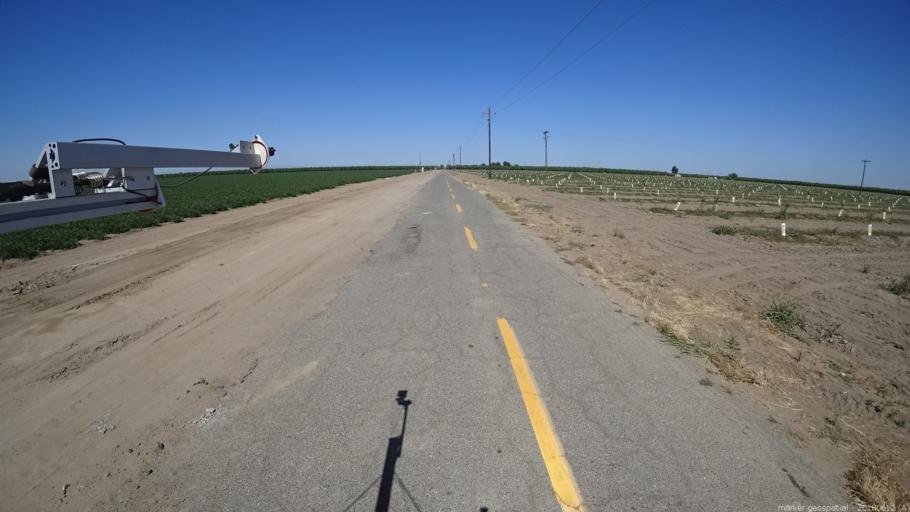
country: US
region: California
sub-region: Madera County
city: Chowchilla
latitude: 37.0324
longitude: -120.3777
